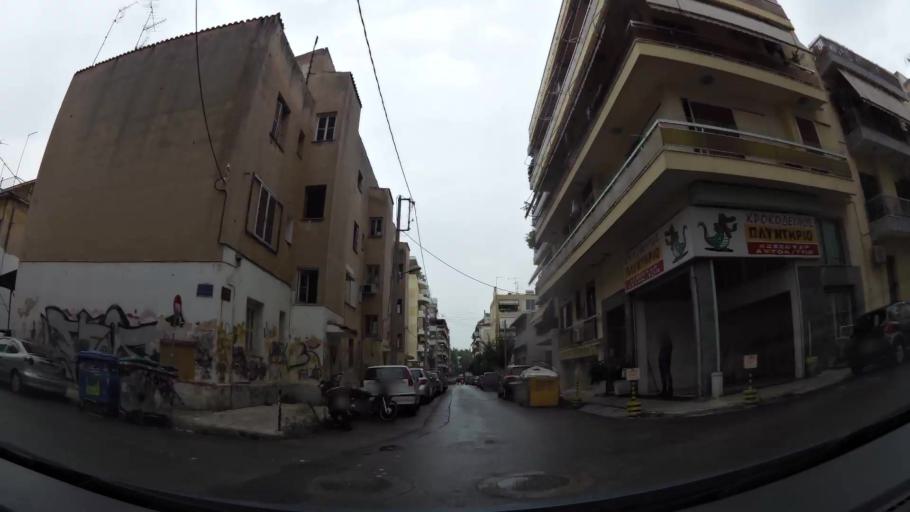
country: GR
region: Attica
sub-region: Nomarchia Athinas
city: Vyronas
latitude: 37.9695
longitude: 23.7558
